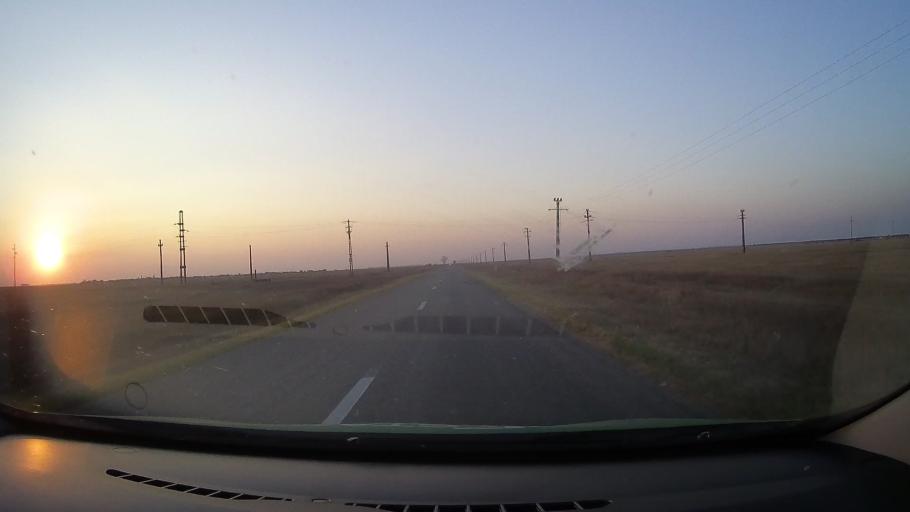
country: RO
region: Arad
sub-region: Comuna Zarand
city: Zarand
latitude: 46.4127
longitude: 21.6290
